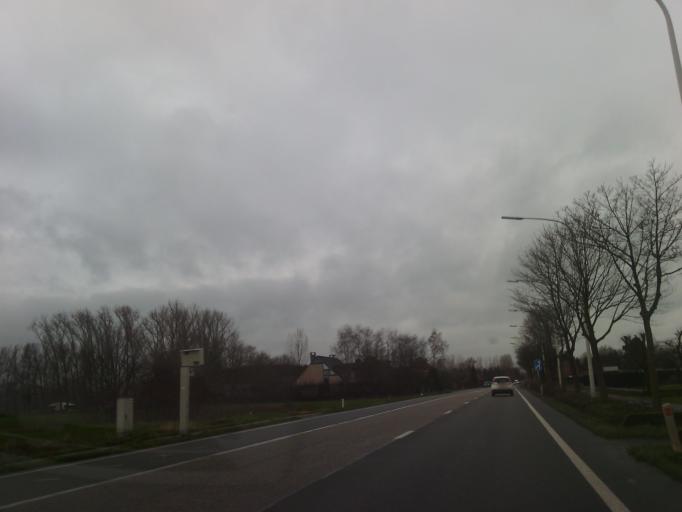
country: BE
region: Flanders
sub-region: Provincie Oost-Vlaanderen
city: Lokeren
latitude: 51.1132
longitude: 3.9386
